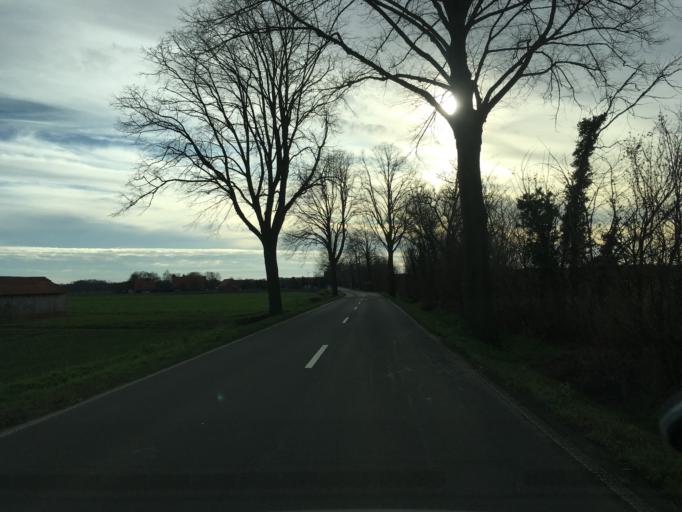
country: DE
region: North Rhine-Westphalia
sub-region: Regierungsbezirk Munster
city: Legden
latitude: 52.0702
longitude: 7.1357
